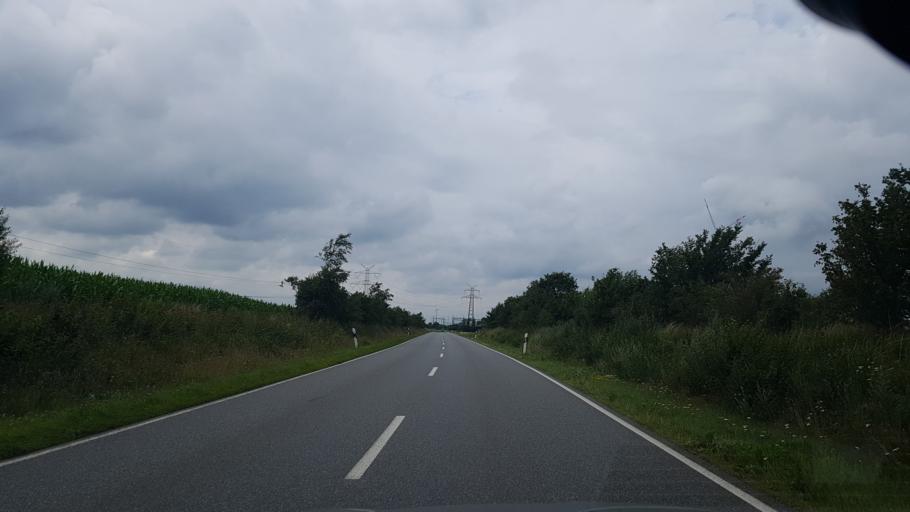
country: DE
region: Schleswig-Holstein
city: Jardelund
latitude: 54.8427
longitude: 9.2086
